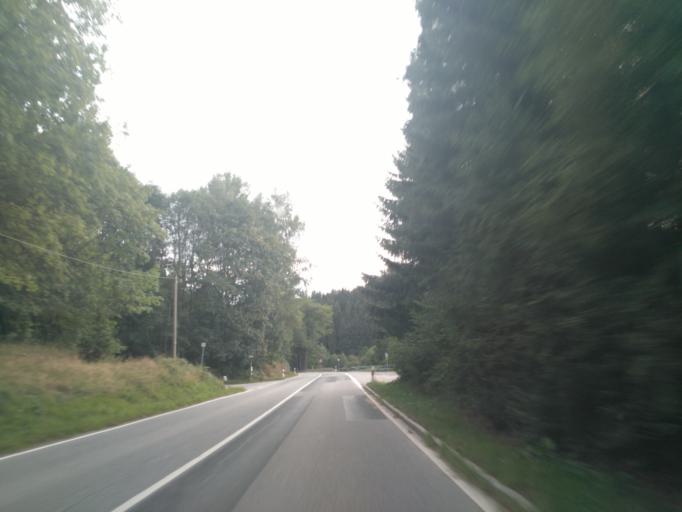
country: DE
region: Saxony
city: Tannenberg
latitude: 50.5814
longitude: 12.9469
